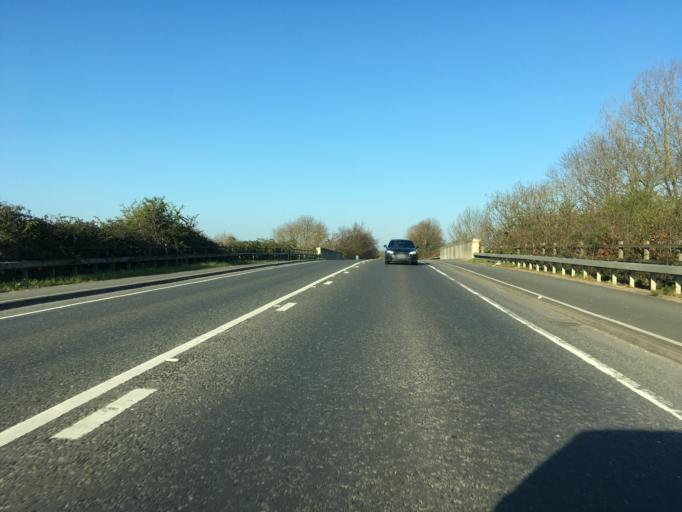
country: GB
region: England
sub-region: Oxfordshire
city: Yarnton
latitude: 51.7914
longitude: -1.3334
